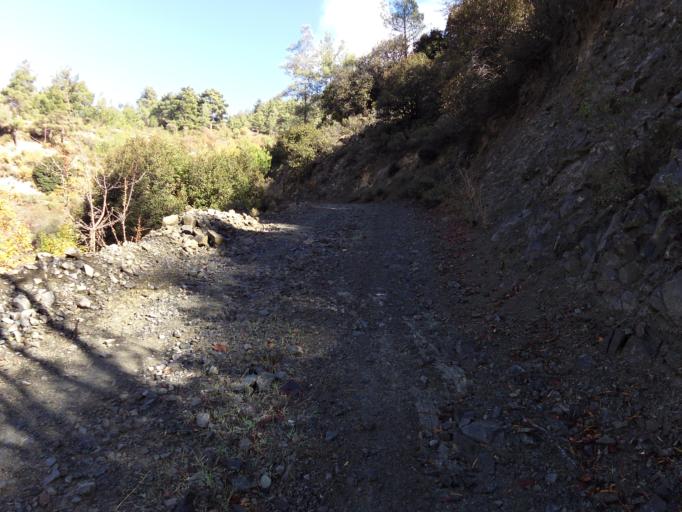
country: CY
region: Limassol
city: Kyperounta
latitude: 34.9290
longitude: 32.9463
